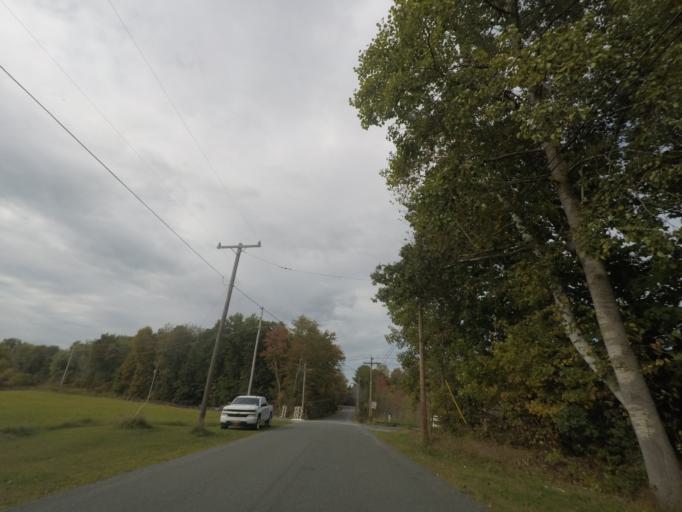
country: US
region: New York
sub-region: Rensselaer County
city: Nassau
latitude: 42.5549
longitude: -73.6250
